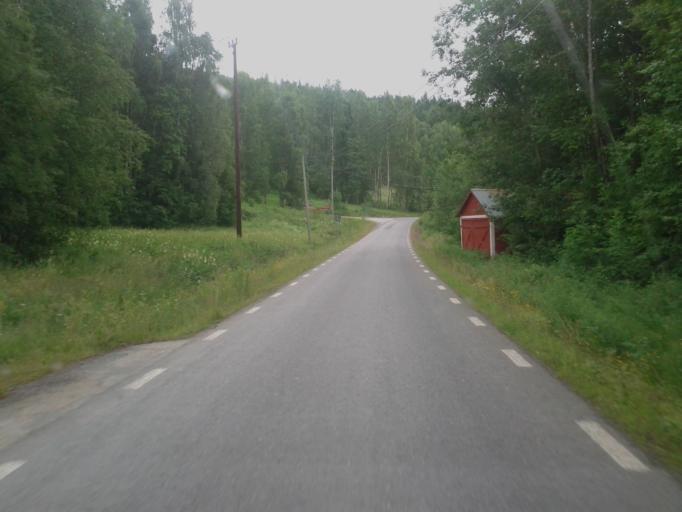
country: SE
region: Vaesternorrland
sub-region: OErnskoeldsviks Kommun
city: Bjasta
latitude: 63.0669
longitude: 18.4253
